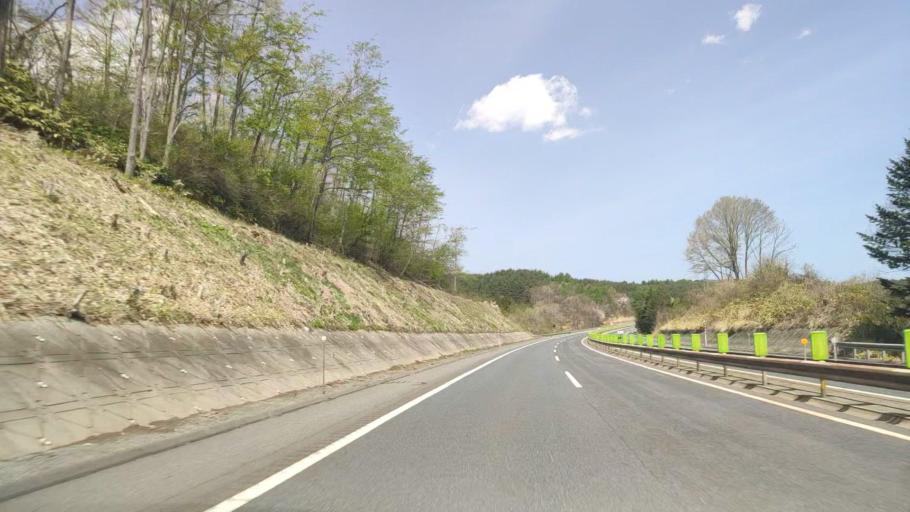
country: JP
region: Aomori
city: Hachinohe
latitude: 40.4205
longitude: 141.4395
